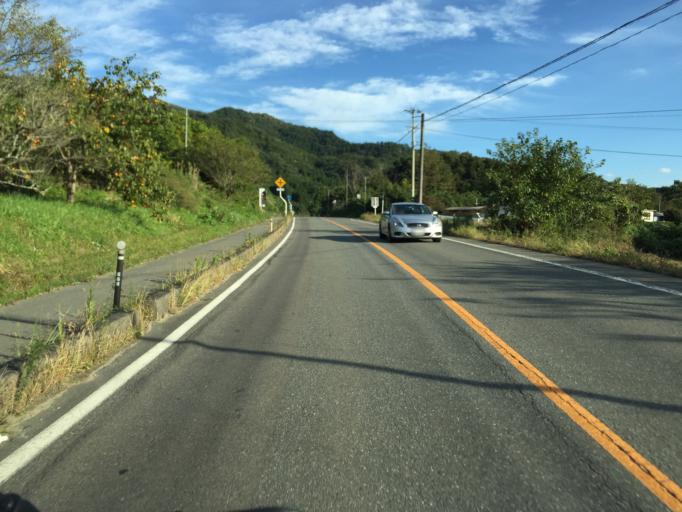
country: JP
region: Fukushima
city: Hobaramachi
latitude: 37.7136
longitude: 140.6066
